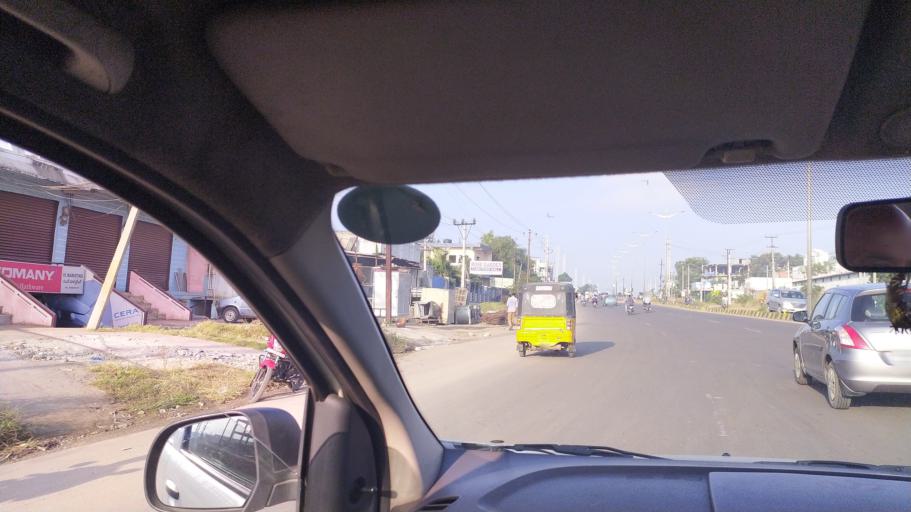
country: IN
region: Telangana
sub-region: Rangareddi
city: Balapur
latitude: 17.3151
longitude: 78.4580
